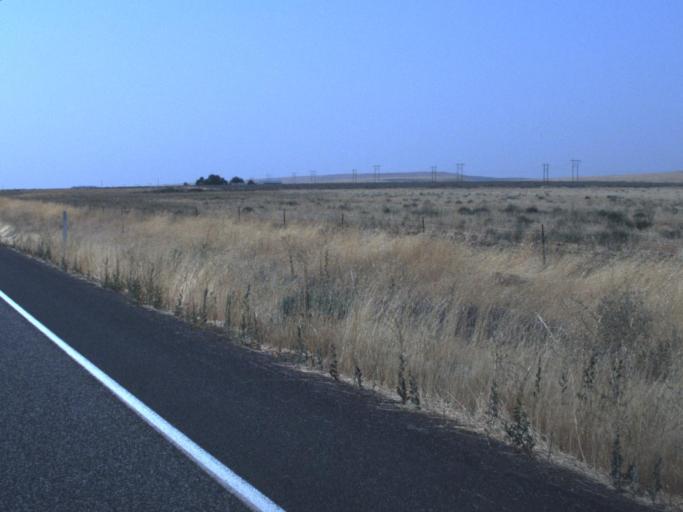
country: US
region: Washington
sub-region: Grant County
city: Desert Aire
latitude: 46.5194
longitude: -120.0142
